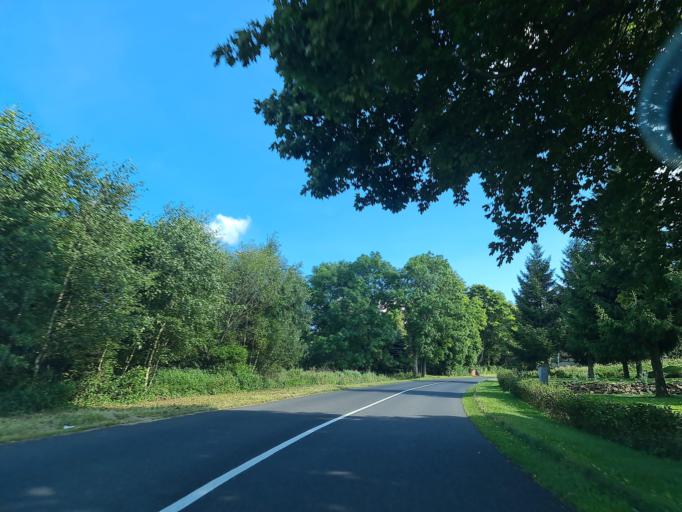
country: DE
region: Saxony
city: Deutschneudorf
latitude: 50.6280
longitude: 13.5032
